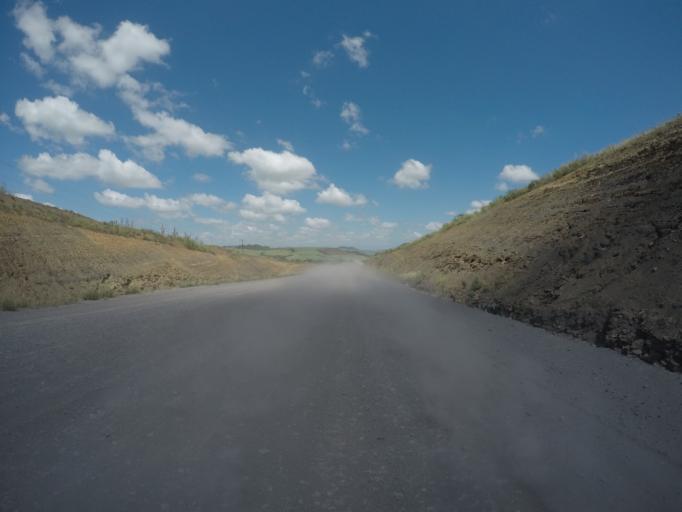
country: ZA
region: KwaZulu-Natal
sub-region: uThungulu District Municipality
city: Empangeni
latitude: -28.6347
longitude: 31.7624
